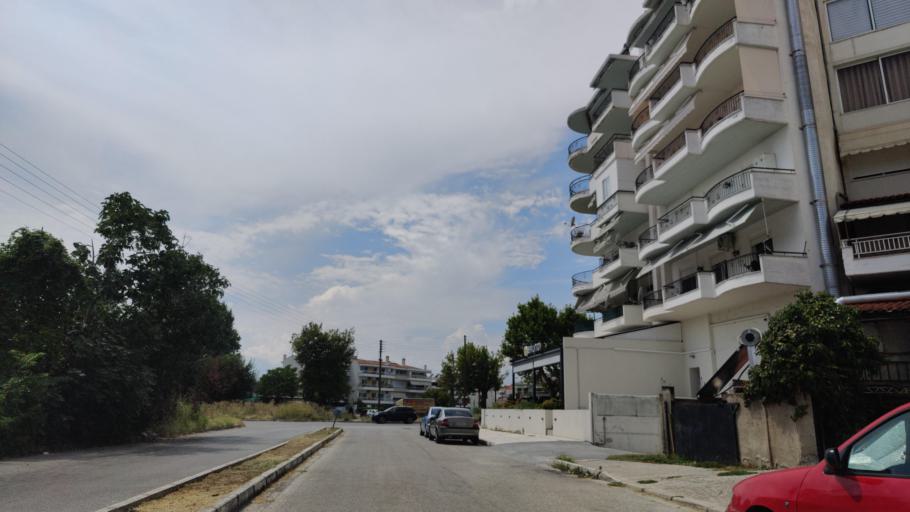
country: GR
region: Central Macedonia
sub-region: Nomos Serron
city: Serres
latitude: 41.0804
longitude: 23.5421
